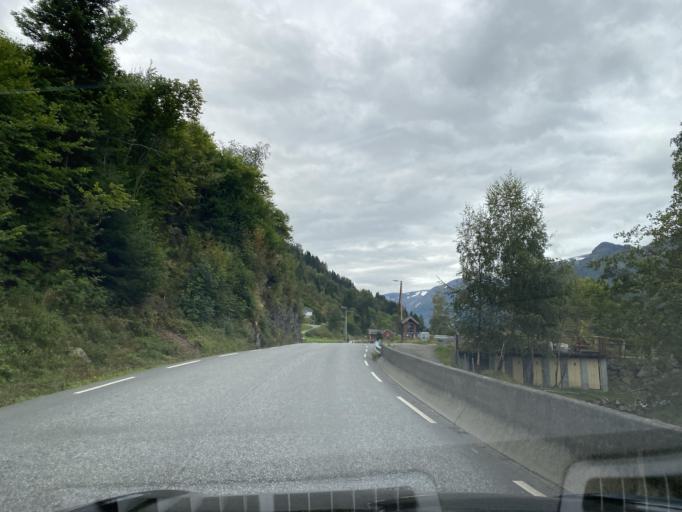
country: NO
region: Hordaland
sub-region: Odda
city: Odda
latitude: 60.2287
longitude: 6.6103
